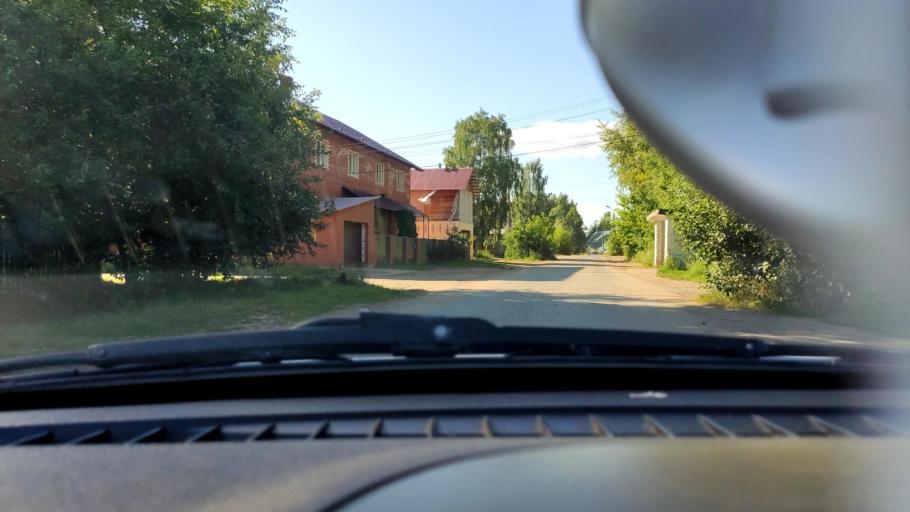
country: RU
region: Perm
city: Krasnokamsk
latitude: 58.0783
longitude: 55.8111
